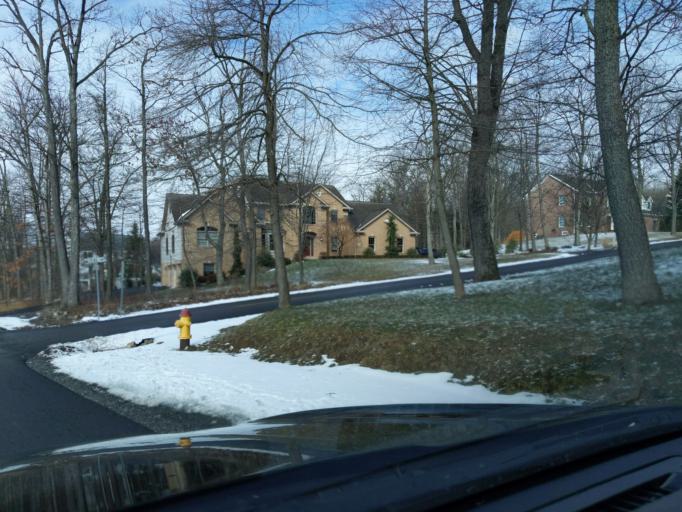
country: US
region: Pennsylvania
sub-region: Blair County
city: Lakemont
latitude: 40.4723
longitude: -78.3770
